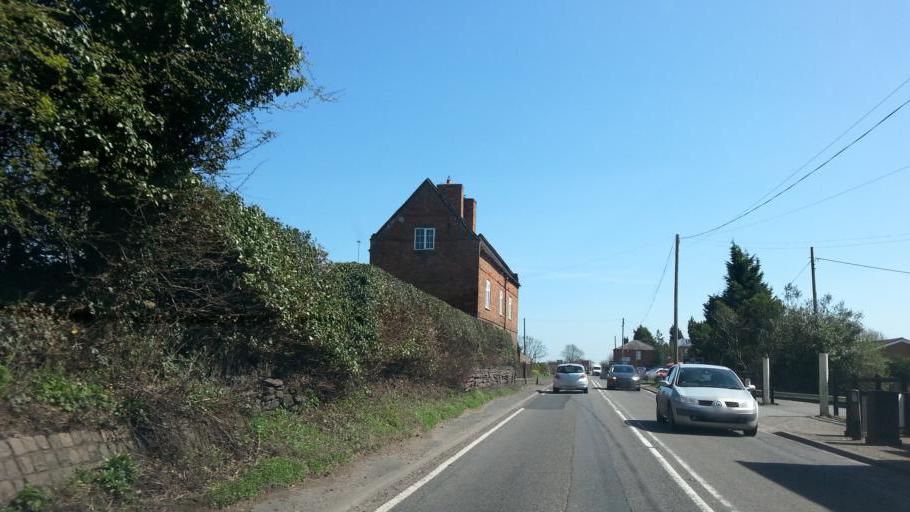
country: GB
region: England
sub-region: Staffordshire
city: Brewood
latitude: 52.6943
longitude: -2.1751
